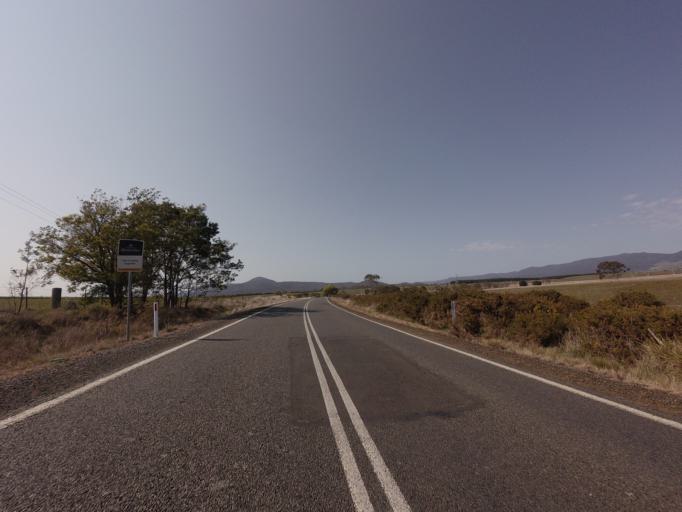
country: AU
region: Tasmania
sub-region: Northern Midlands
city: Evandale
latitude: -41.7994
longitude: 147.6984
